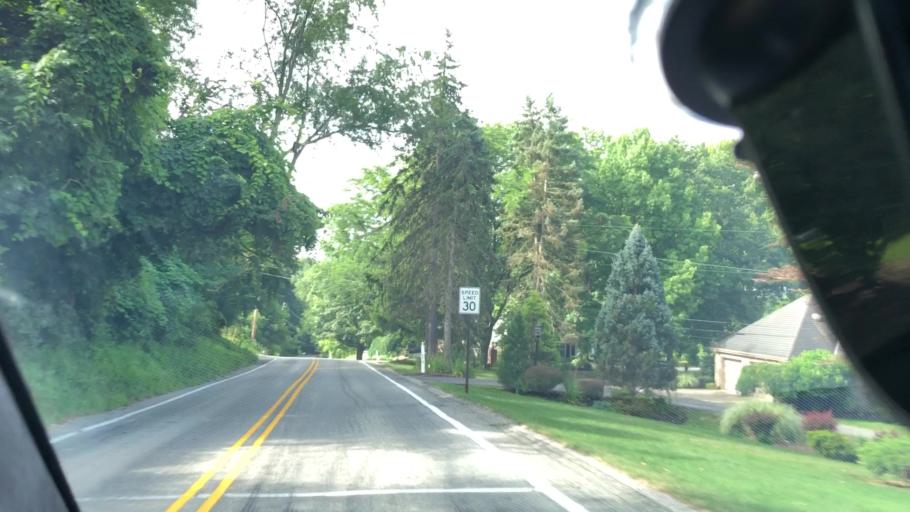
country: US
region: Pennsylvania
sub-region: Allegheny County
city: Upper Saint Clair
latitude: 40.3531
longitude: -80.0738
